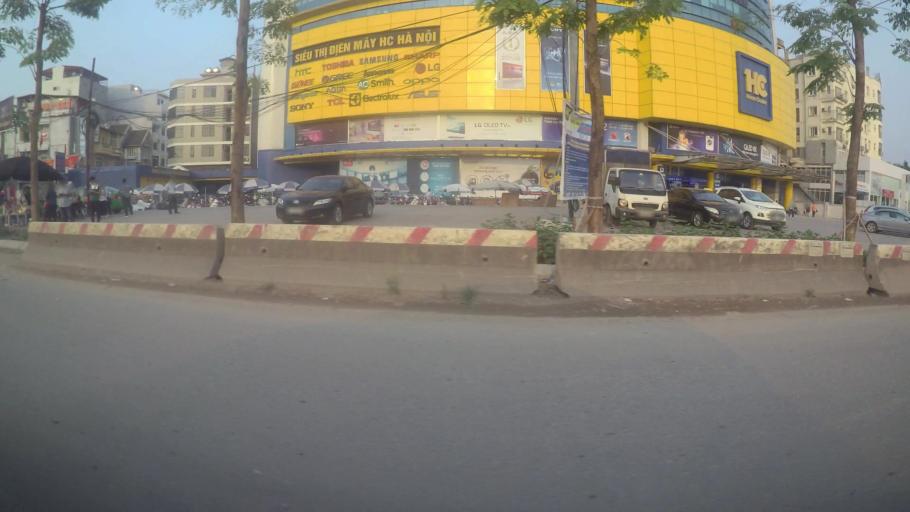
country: VN
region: Ha Noi
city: Tay Ho
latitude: 21.0693
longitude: 105.7855
